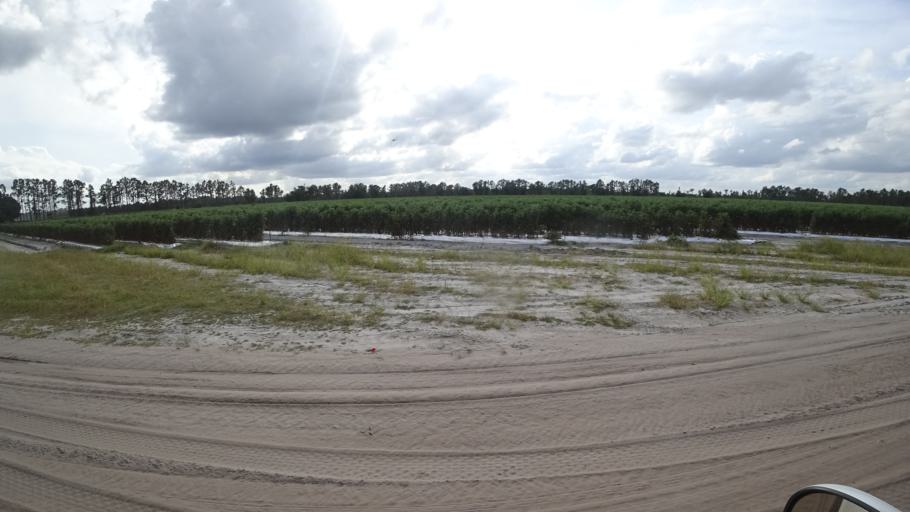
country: US
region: Florida
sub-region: Hillsborough County
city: Balm
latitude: 27.6198
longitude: -82.1338
